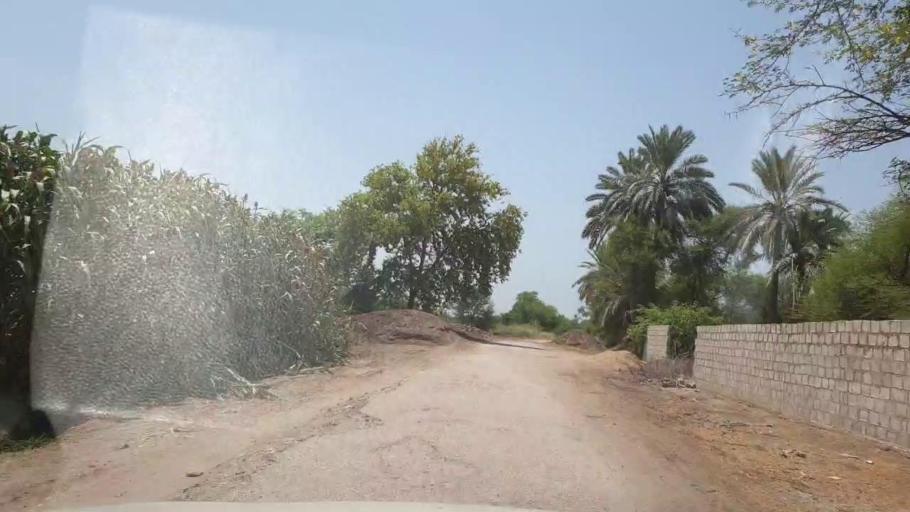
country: PK
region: Sindh
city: Bozdar
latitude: 27.1265
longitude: 68.6294
